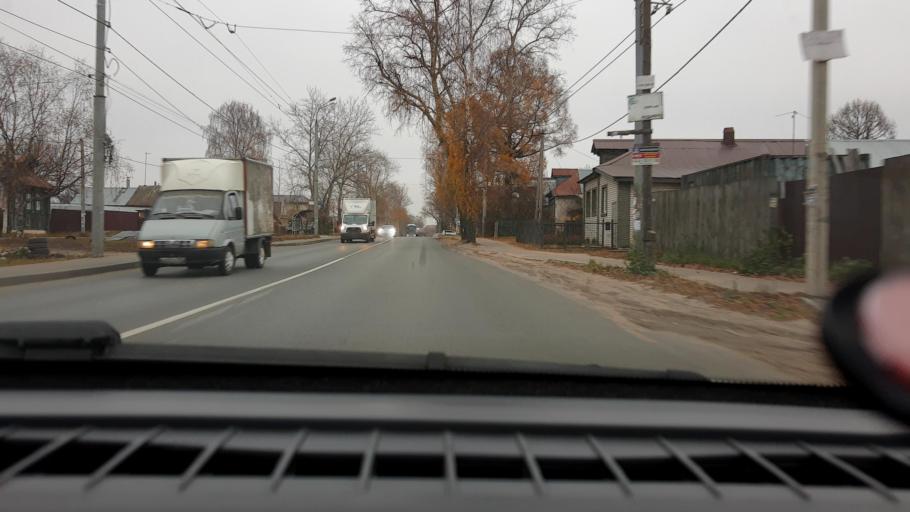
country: RU
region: Nizjnij Novgorod
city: Lukino
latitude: 56.3886
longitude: 43.7459
